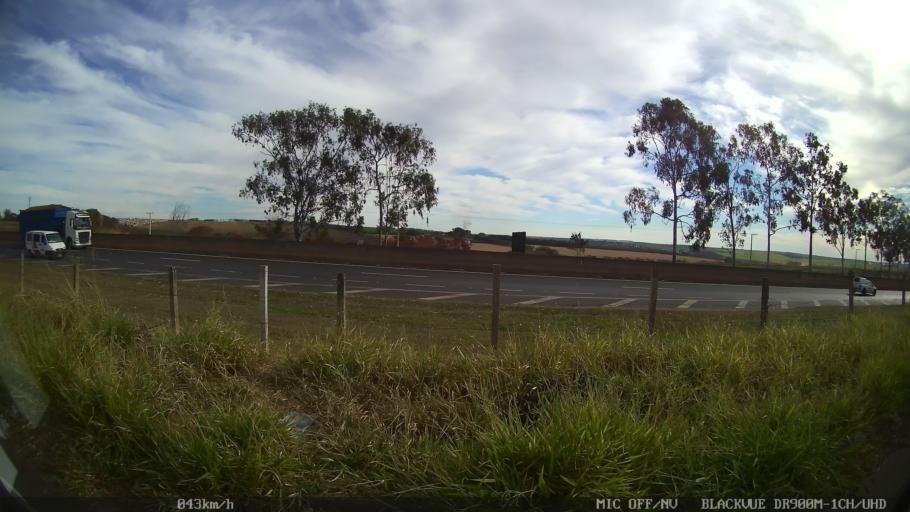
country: BR
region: Sao Paulo
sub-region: Catanduva
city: Catanduva
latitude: -21.1258
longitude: -49.0011
